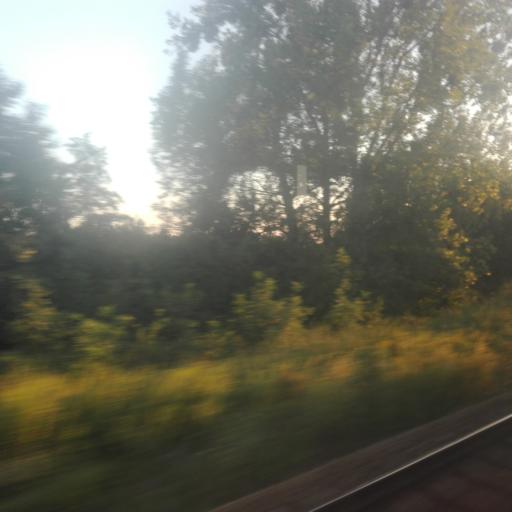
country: PL
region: Masovian Voivodeship
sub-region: Powiat warszawski zachodni
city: Bieniewice
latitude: 52.1861
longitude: 20.5607
